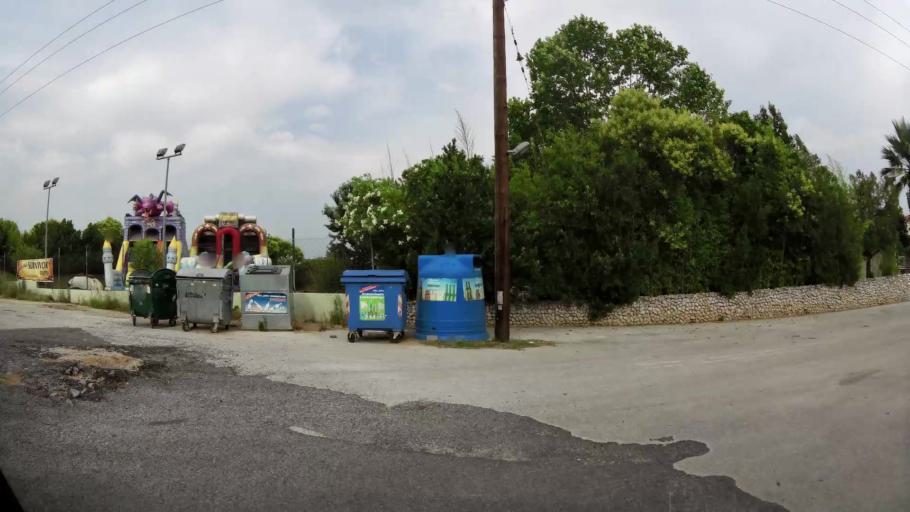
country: GR
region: Central Macedonia
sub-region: Nomos Thessalonikis
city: Oraiokastro
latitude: 40.7149
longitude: 22.9295
